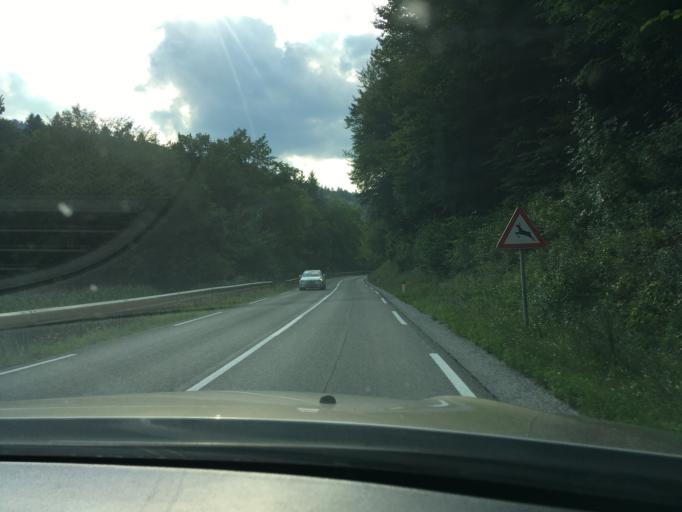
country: SI
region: Dolenjske Toplice
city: Dolenjske Toplice
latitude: 45.7815
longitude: 15.0053
